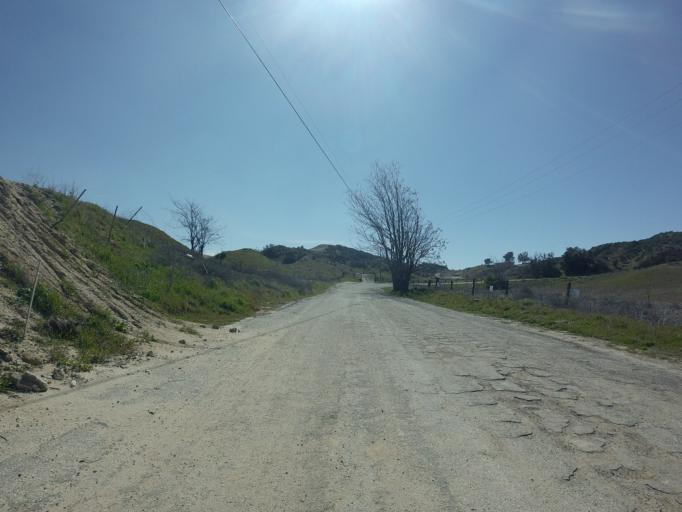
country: US
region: California
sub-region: Riverside County
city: Beaumont
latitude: 33.9322
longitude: -117.0346
